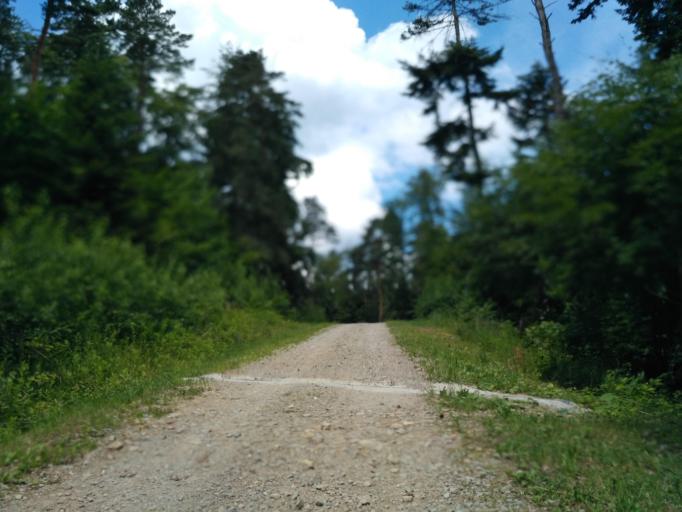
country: PL
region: Subcarpathian Voivodeship
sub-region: Powiat jasielski
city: Brzyska
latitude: 49.8047
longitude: 21.3707
